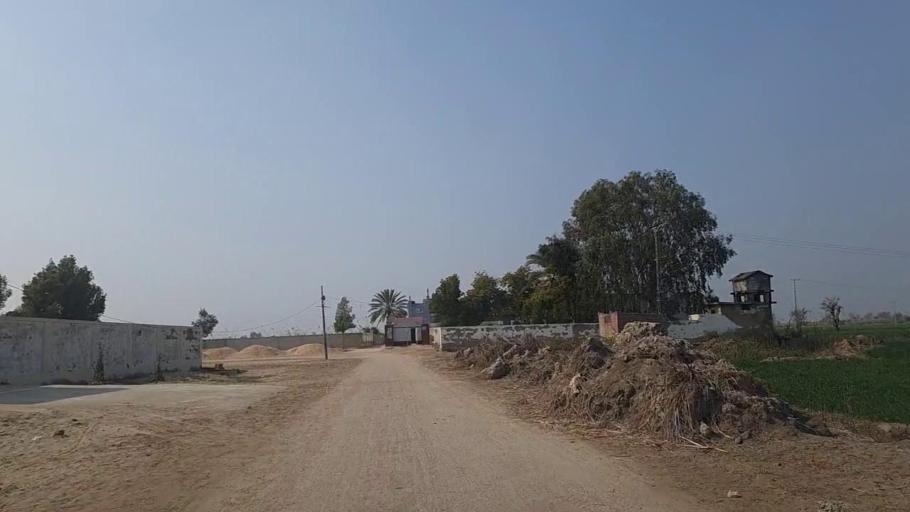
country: PK
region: Sindh
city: Daur
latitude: 26.4489
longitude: 68.4435
